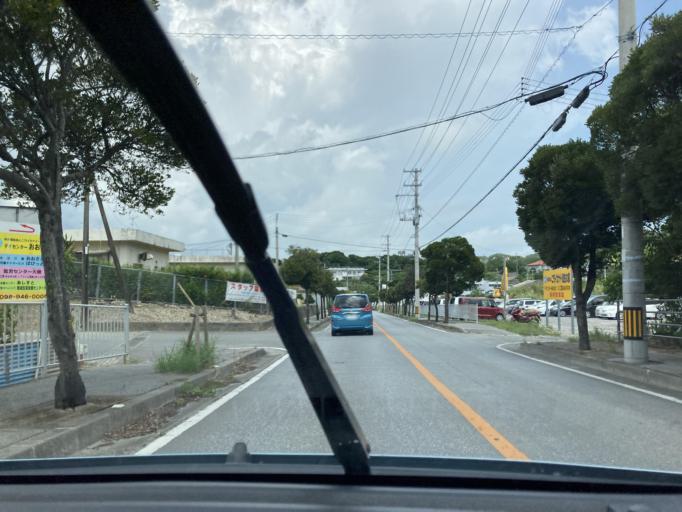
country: JP
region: Okinawa
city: Tomigusuku
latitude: 26.1687
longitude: 127.7543
